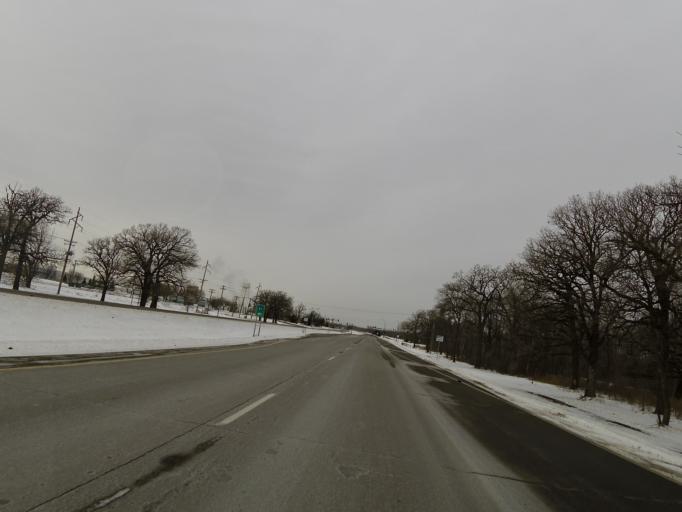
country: US
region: Minnesota
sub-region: Hennepin County
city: Eden Prairie
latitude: 44.7995
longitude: -93.4656
